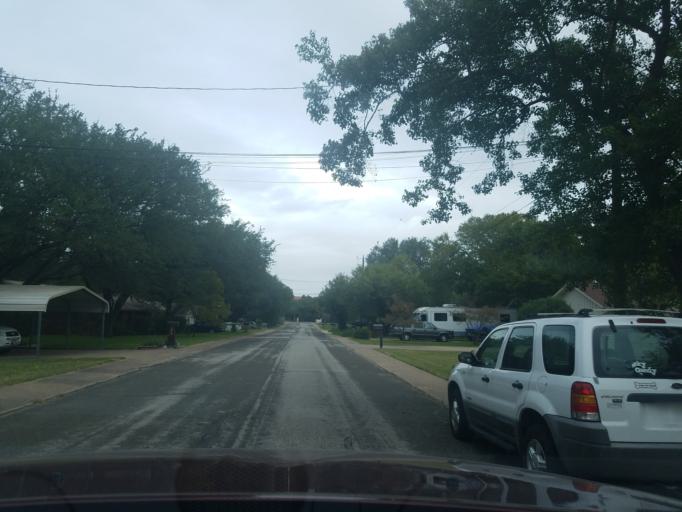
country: US
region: Texas
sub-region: Williamson County
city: Anderson Mill
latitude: 30.4806
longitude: -97.8069
